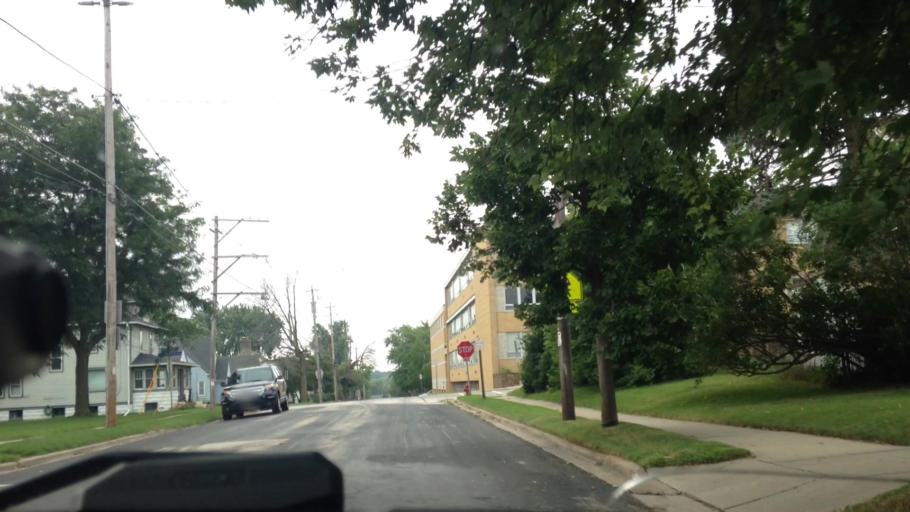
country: US
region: Wisconsin
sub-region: Waukesha County
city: Menomonee Falls
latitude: 43.1814
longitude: -88.1109
